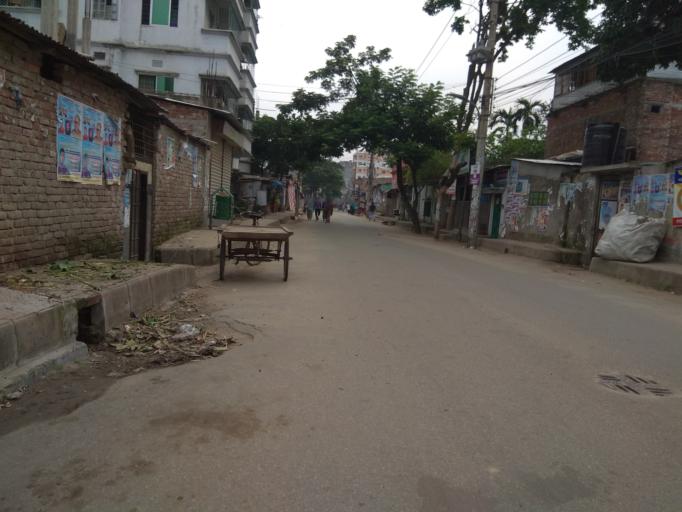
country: BD
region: Dhaka
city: Azimpur
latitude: 23.7106
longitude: 90.3695
